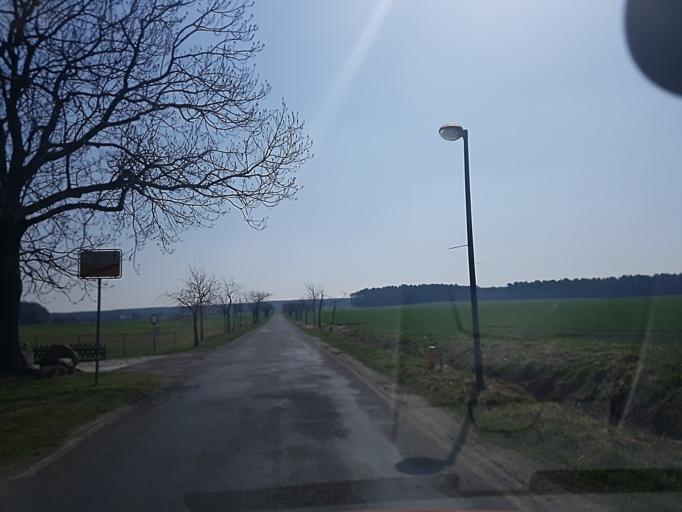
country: DE
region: Saxony
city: Gross Duben
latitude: 51.6728
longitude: 14.5378
